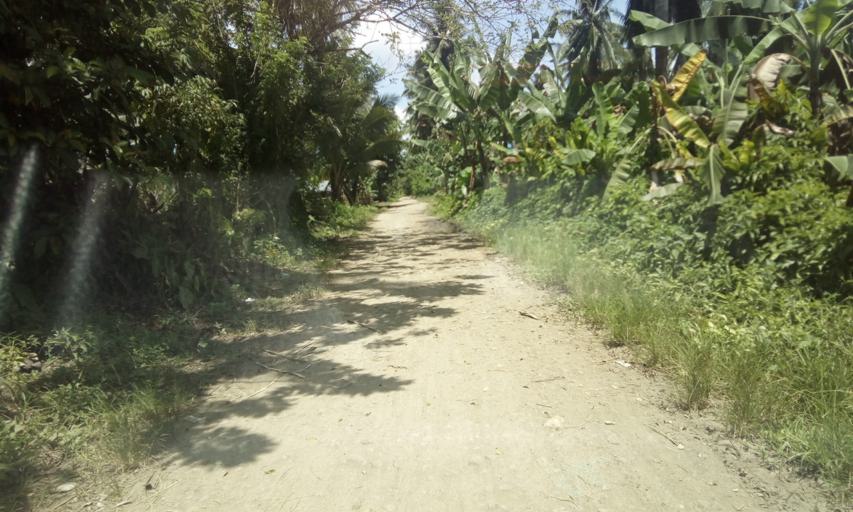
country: PH
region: Caraga
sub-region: Province of Agusan del Sur
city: Santa Josefa
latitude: 7.9518
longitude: 125.9985
